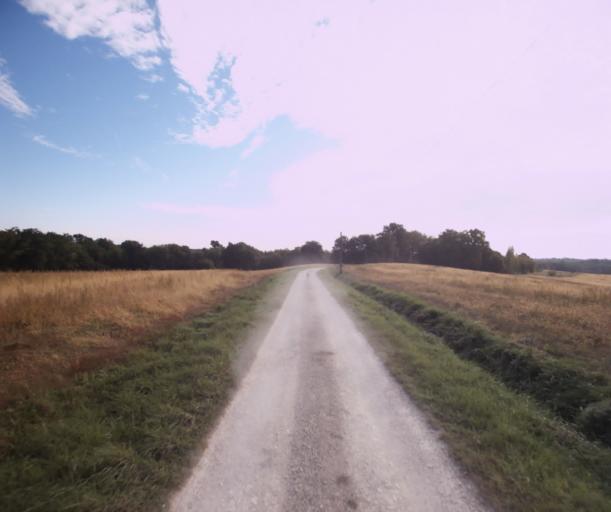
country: FR
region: Midi-Pyrenees
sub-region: Departement du Gers
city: Eauze
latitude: 43.8964
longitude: 0.0405
